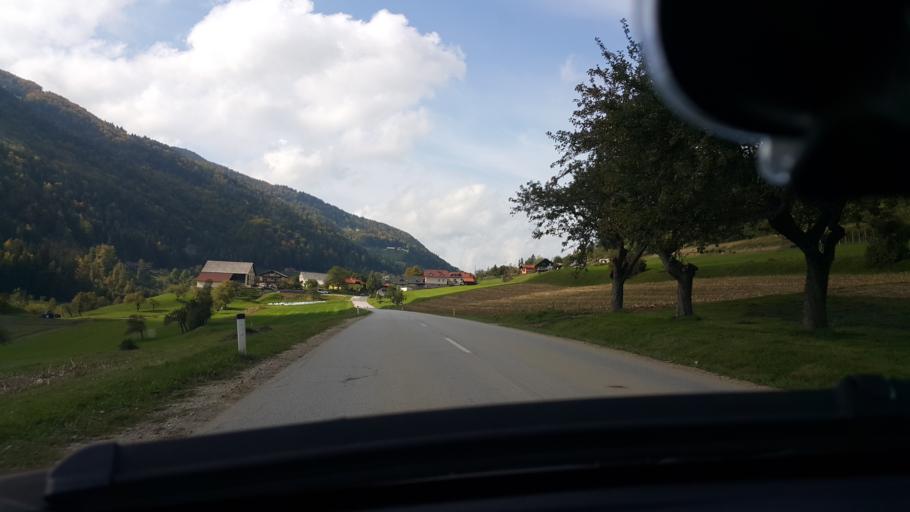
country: SI
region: Zrece
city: Zrece
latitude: 46.3661
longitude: 15.3560
